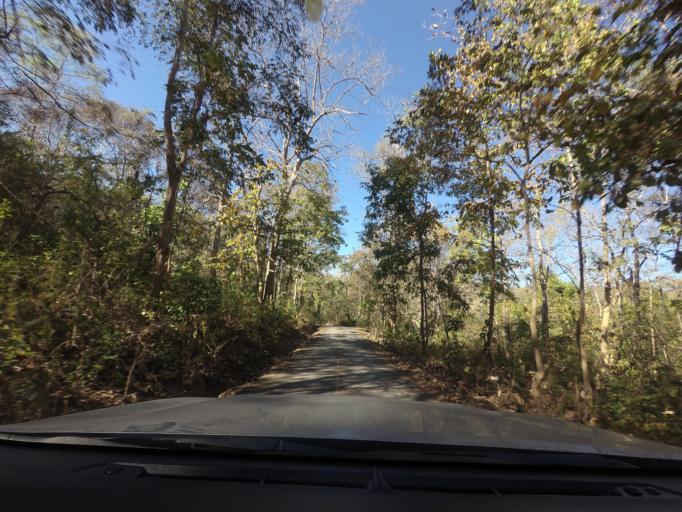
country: TH
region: Mae Hong Son
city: Wiang Nuea
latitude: 19.4011
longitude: 98.4183
